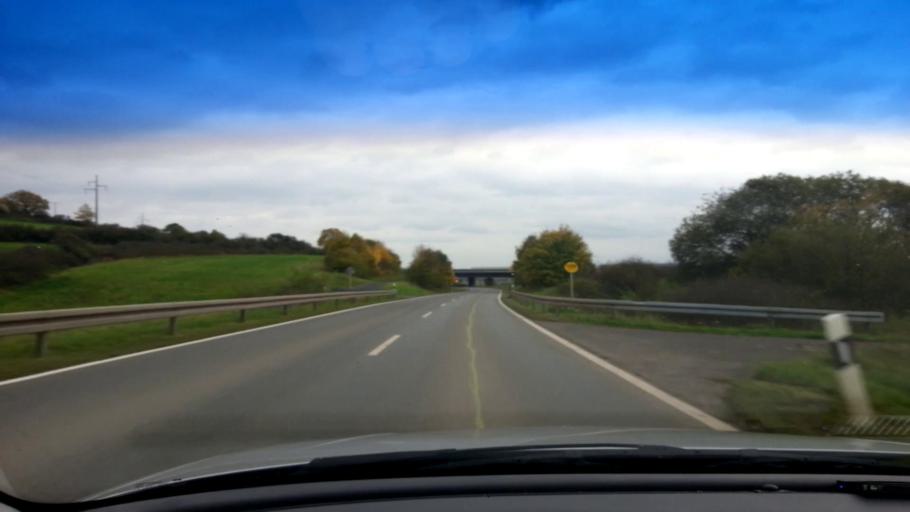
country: DE
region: Bavaria
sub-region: Regierungsbezirk Unterfranken
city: Stettfeld
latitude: 49.9632
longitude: 10.7299
